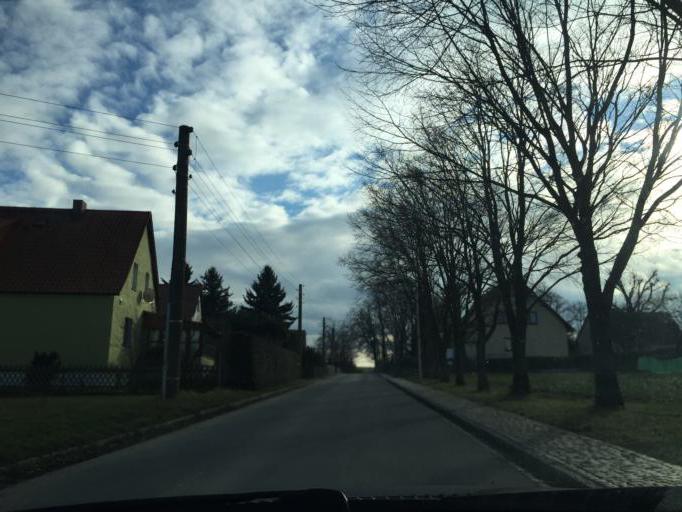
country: DE
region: Saxony
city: Ebersbach
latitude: 51.2285
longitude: 13.6620
